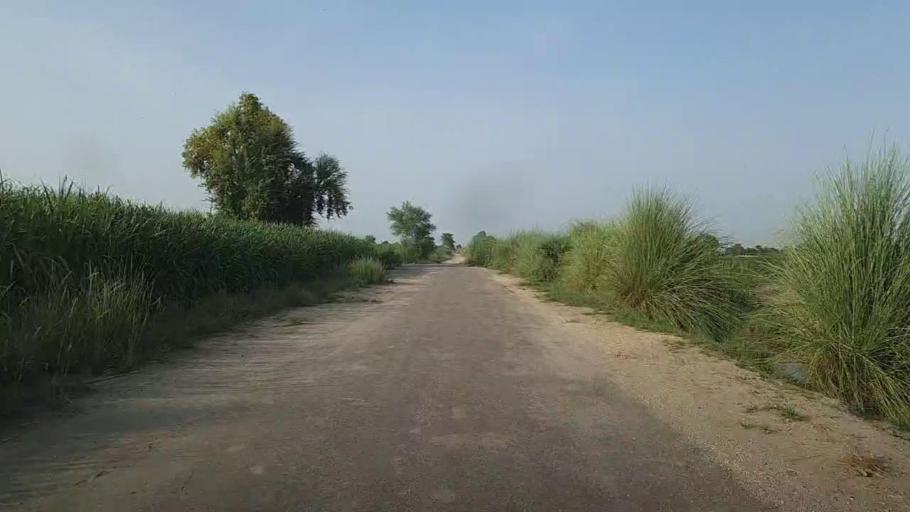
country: PK
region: Sindh
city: Ubauro
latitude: 28.0992
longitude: 69.8234
